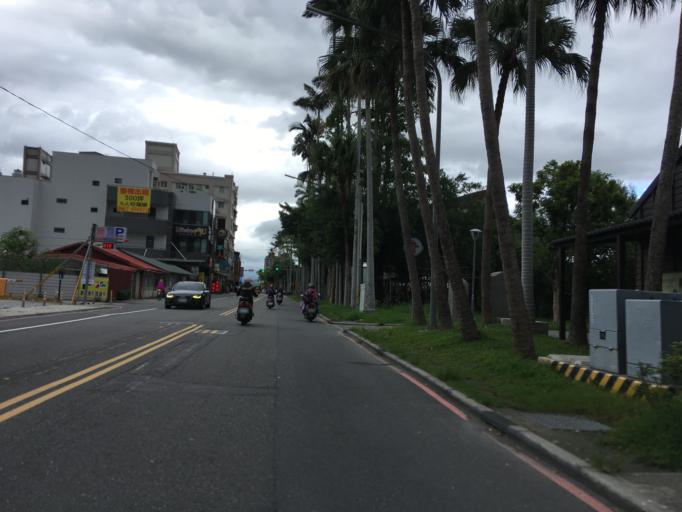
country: TW
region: Taiwan
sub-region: Yilan
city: Yilan
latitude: 24.6828
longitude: 121.7714
